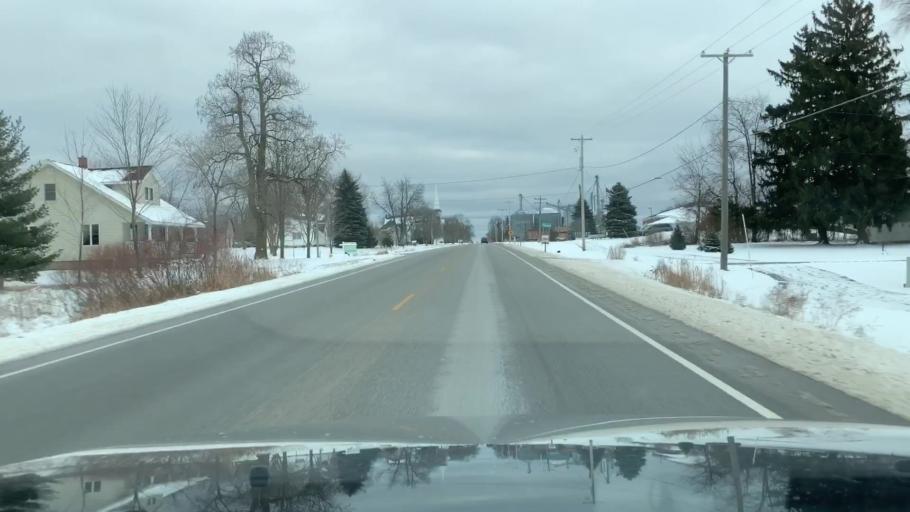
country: US
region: Michigan
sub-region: Ottawa County
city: Zeeland
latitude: 42.8119
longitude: -85.9459
